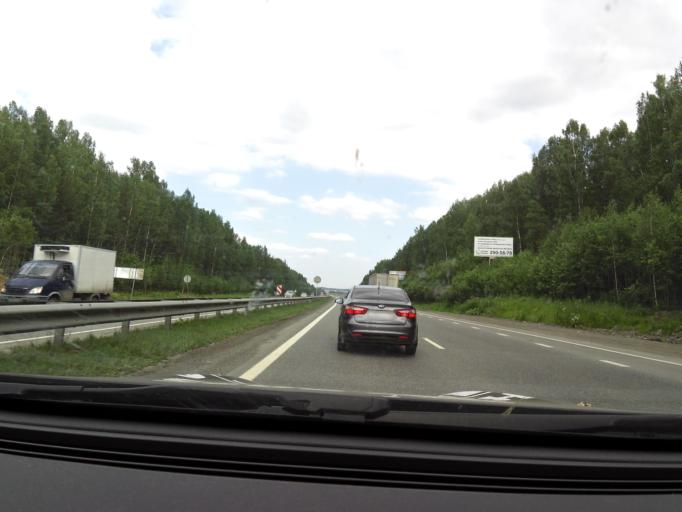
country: RU
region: Sverdlovsk
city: Talitsa
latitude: 56.8385
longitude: 60.1221
